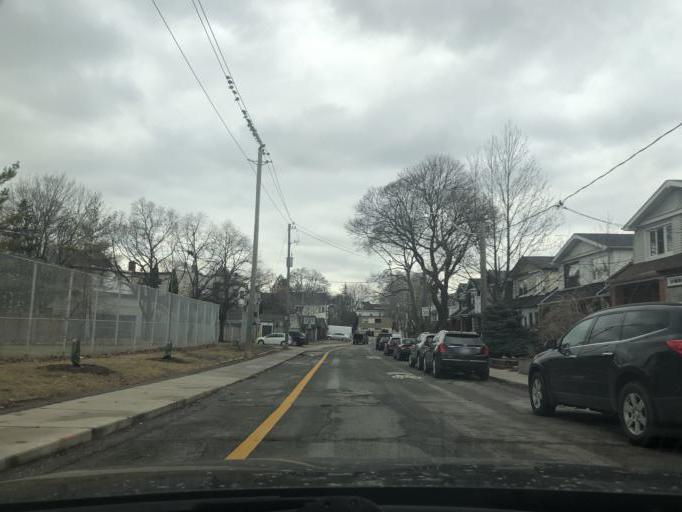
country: CA
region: Ontario
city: Toronto
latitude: 43.6795
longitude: -79.3379
